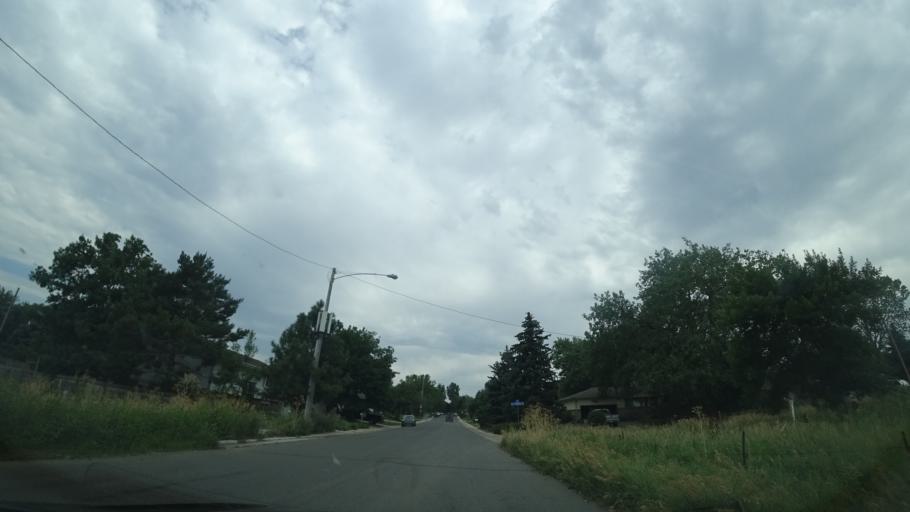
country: US
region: Colorado
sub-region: Jefferson County
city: Lakewood
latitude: 39.7105
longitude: -105.1039
